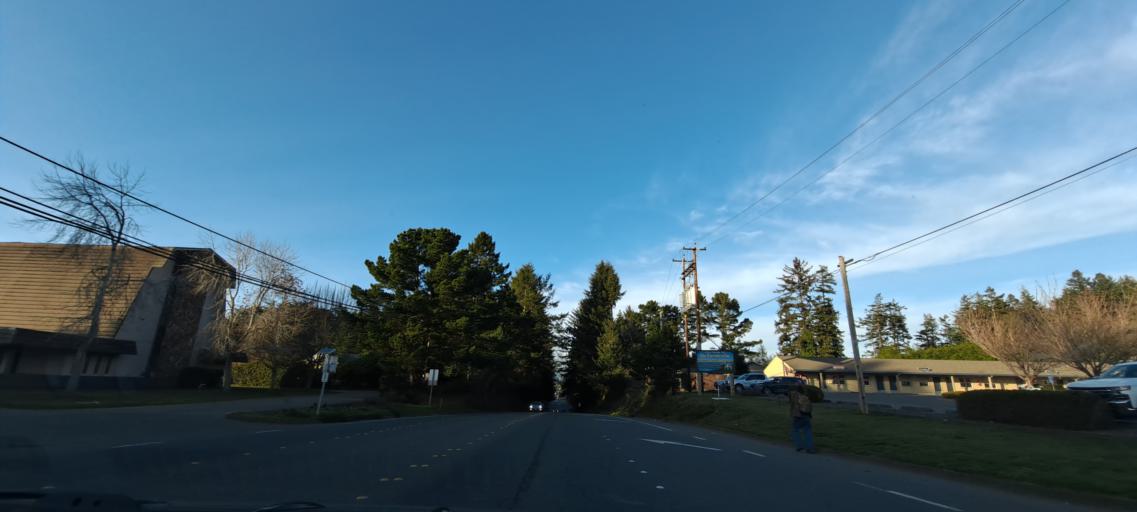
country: US
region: California
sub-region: Humboldt County
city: McKinleyville
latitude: 40.9270
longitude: -124.1008
